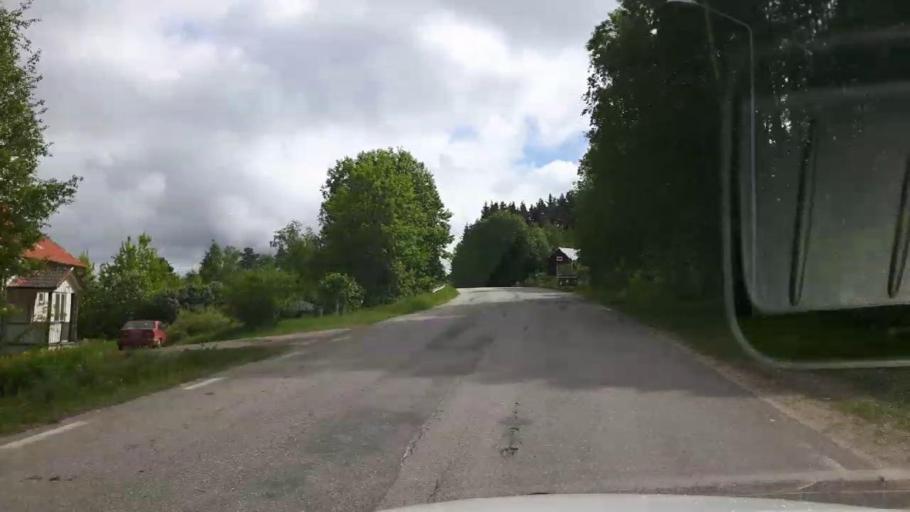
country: SE
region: Gaevleborg
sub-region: Ovanakers Kommun
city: Alfta
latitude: 61.3360
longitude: 15.9634
